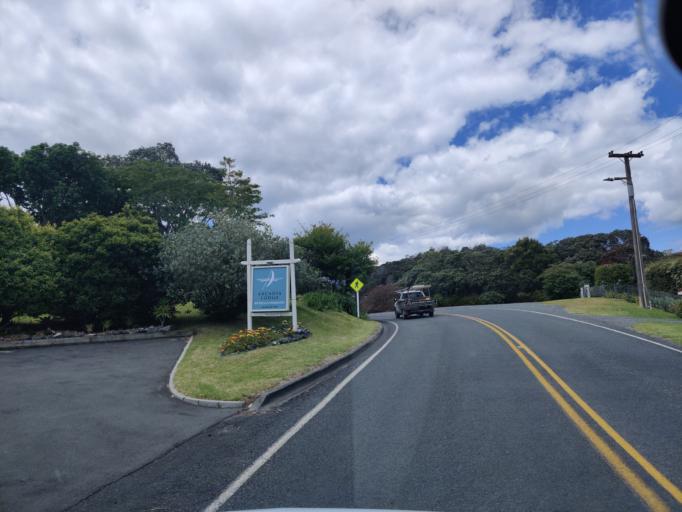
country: NZ
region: Northland
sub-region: Far North District
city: Paihia
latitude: -35.2666
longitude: 174.1260
